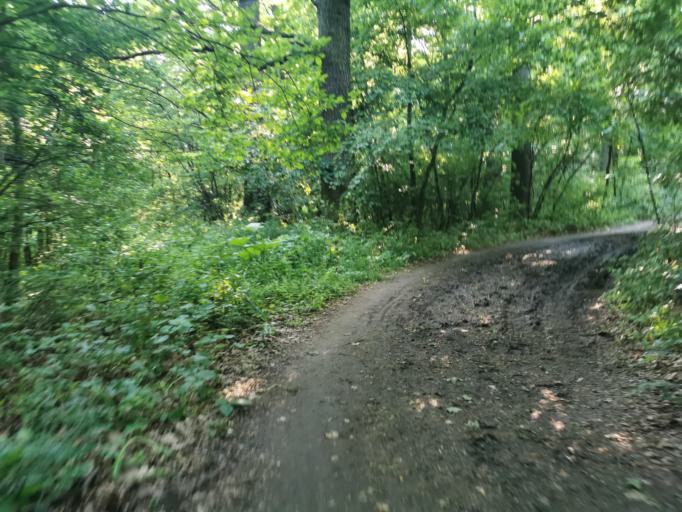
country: CZ
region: South Moravian
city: Knezdub
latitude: 48.8644
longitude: 17.3852
